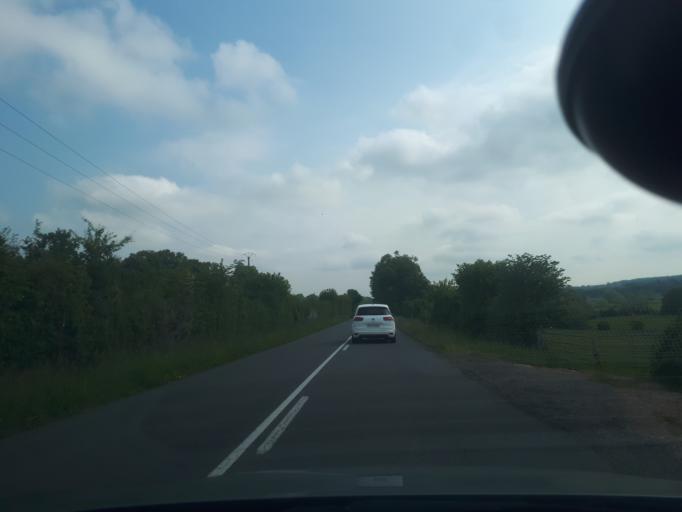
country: FR
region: Auvergne
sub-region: Departement de l'Allier
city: Dompierre-sur-Besbre
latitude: 46.4153
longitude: 3.6100
